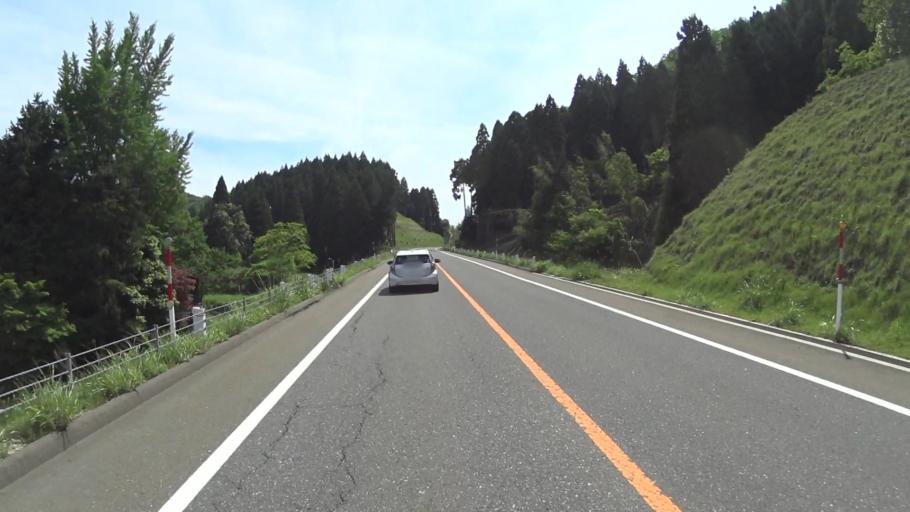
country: JP
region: Fukui
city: Obama
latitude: 35.3981
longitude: 135.9319
